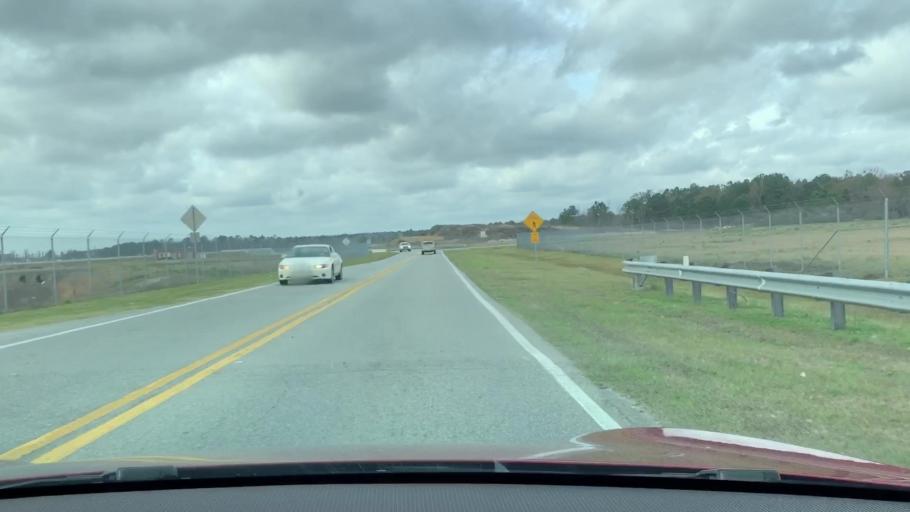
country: US
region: Georgia
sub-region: Chatham County
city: Port Wentworth
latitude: 32.1414
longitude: -81.1994
